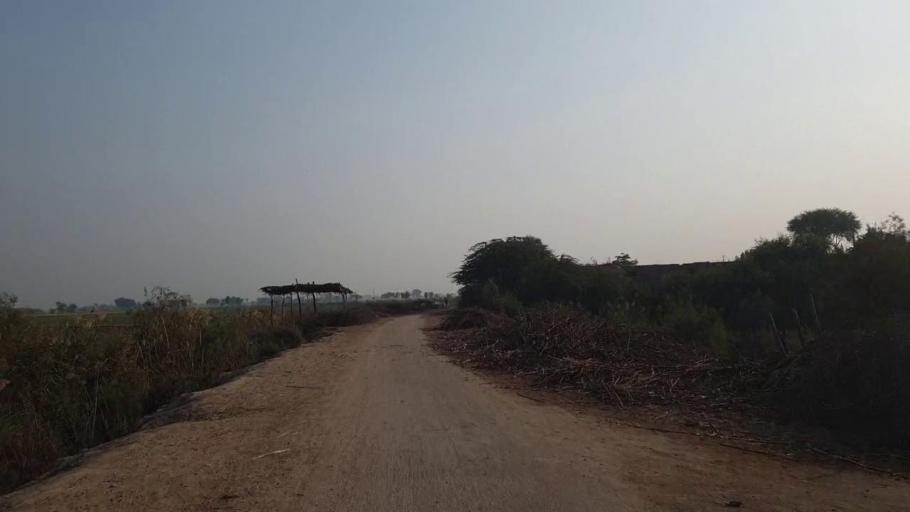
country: PK
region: Sindh
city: Shahdadpur
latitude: 25.9631
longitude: 68.5237
